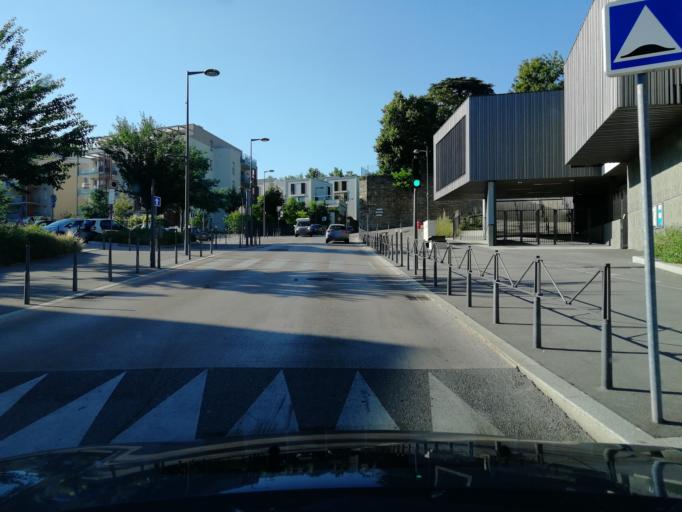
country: FR
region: Rhone-Alpes
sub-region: Departement du Rhone
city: Fontaines-sur-Saone
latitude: 45.8362
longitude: 4.8470
